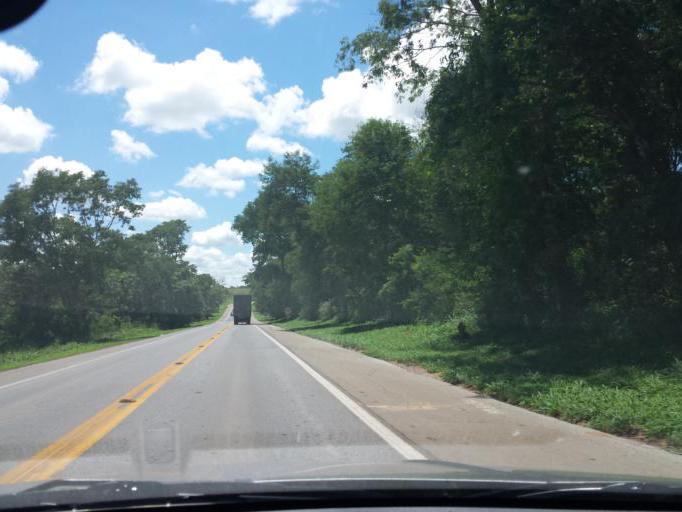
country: BR
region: Goias
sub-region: Cristalina
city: Cristalina
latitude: -16.5311
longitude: -47.8034
